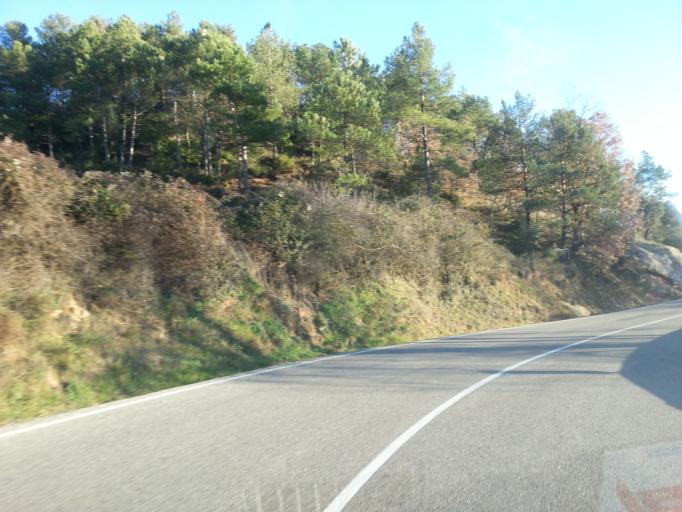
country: ES
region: Catalonia
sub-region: Provincia de Lleida
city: Solsona
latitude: 42.0508
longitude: 1.5109
